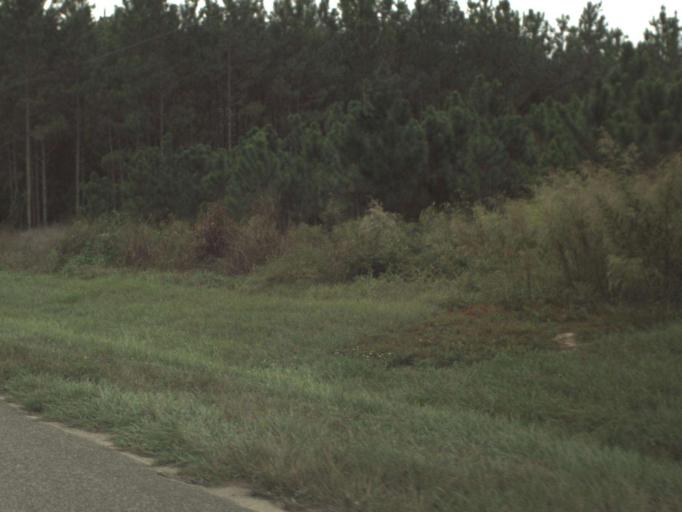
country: US
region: Florida
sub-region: Calhoun County
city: Blountstown
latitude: 30.4623
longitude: -85.0449
